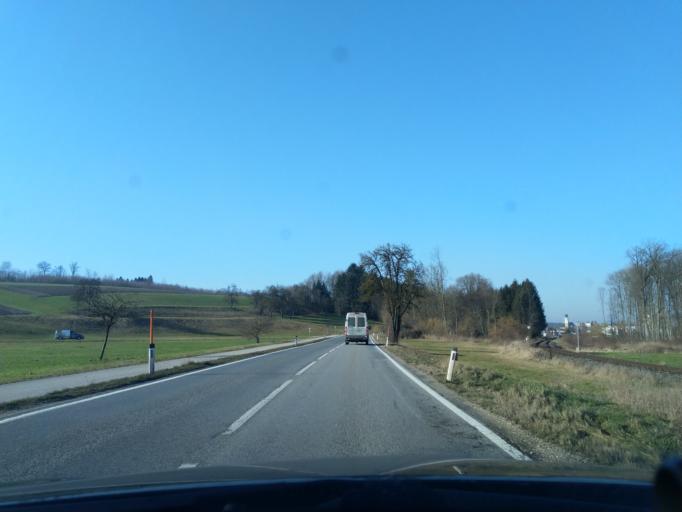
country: AT
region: Upper Austria
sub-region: Politischer Bezirk Ried im Innkreis
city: Ried im Innkreis
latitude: 48.2382
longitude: 13.4622
